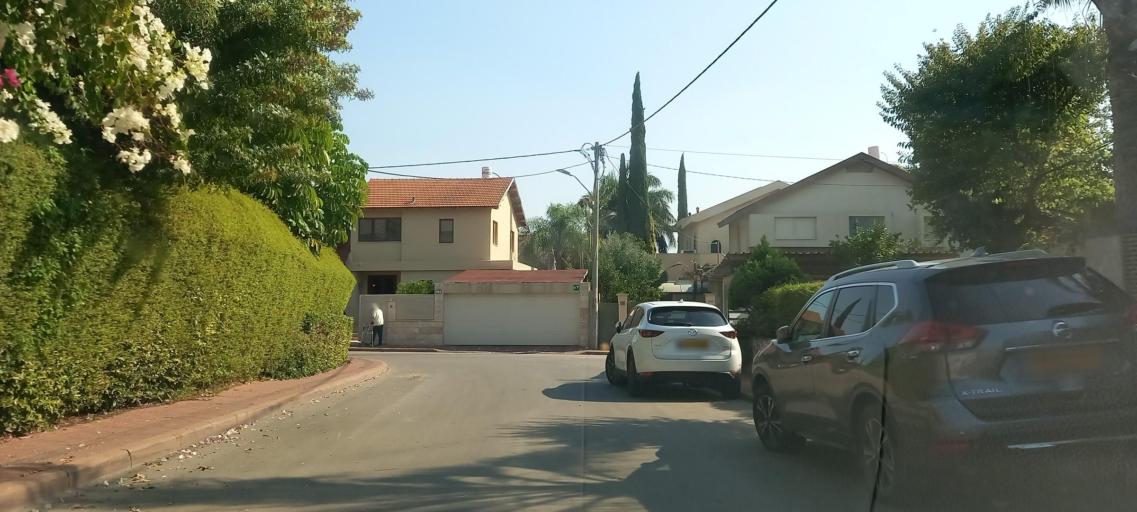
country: IL
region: Tel Aviv
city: Or Yehuda
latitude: 32.0443
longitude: 34.8332
